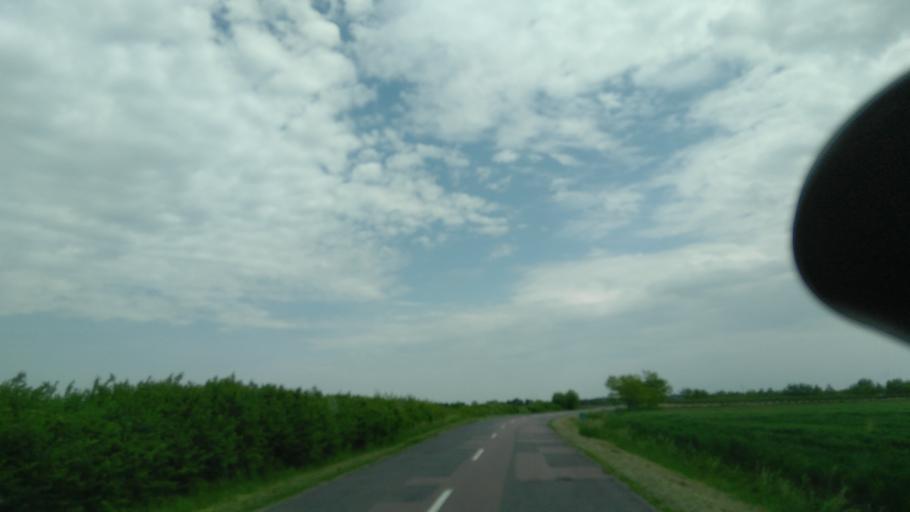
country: HU
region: Hajdu-Bihar
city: Komadi
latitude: 47.0235
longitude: 21.5699
